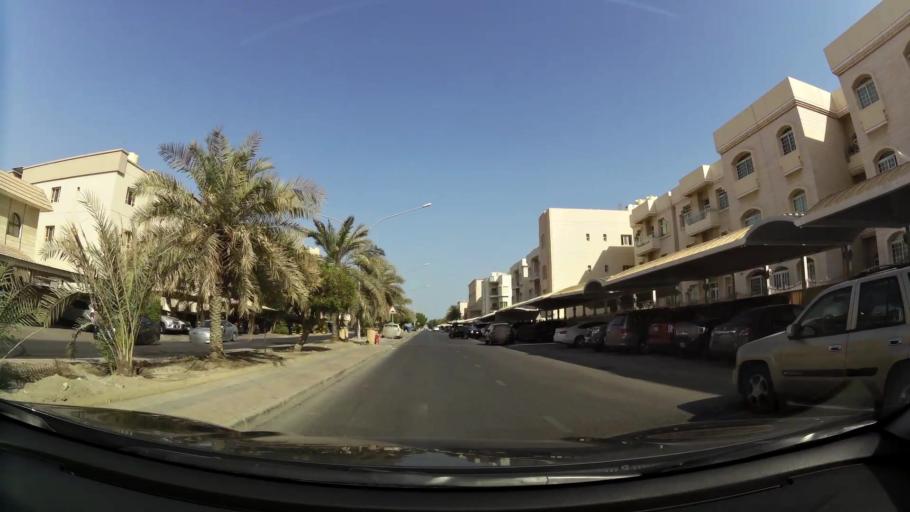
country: KW
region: Muhafazat Hawalli
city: Salwa
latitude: 29.2901
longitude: 48.0809
